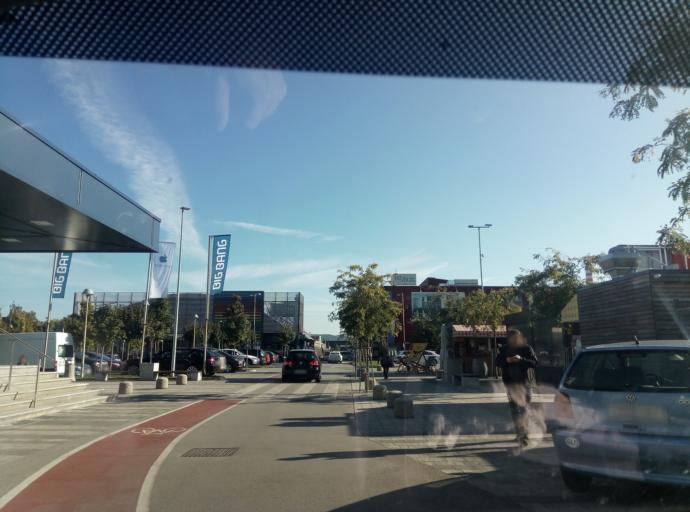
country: SI
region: Ljubljana
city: Ljubljana
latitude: 46.0638
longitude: 14.5452
